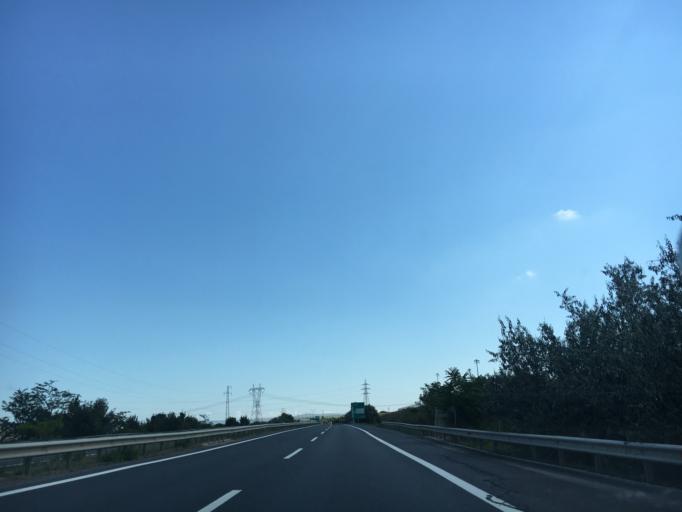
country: TR
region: Istanbul
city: Canta
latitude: 41.0881
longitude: 28.1401
